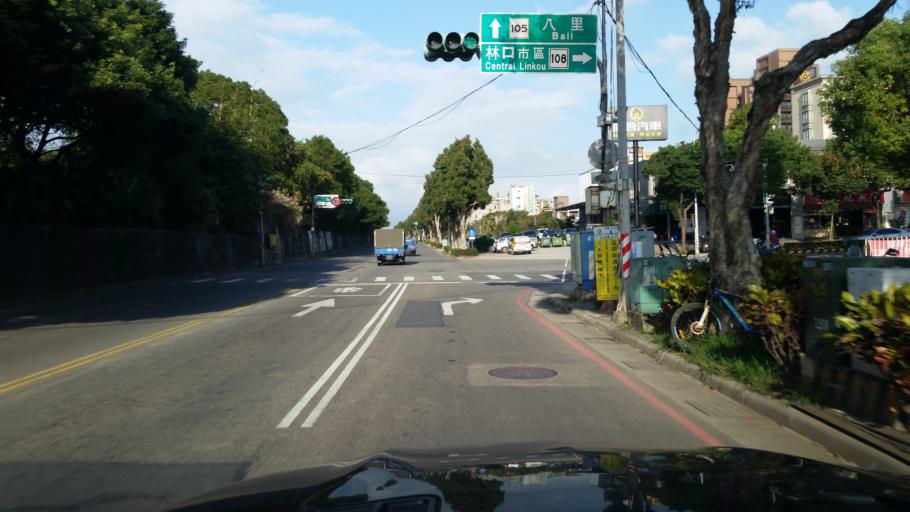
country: TW
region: Taiwan
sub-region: Taoyuan
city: Taoyuan
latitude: 25.0806
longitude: 121.3688
